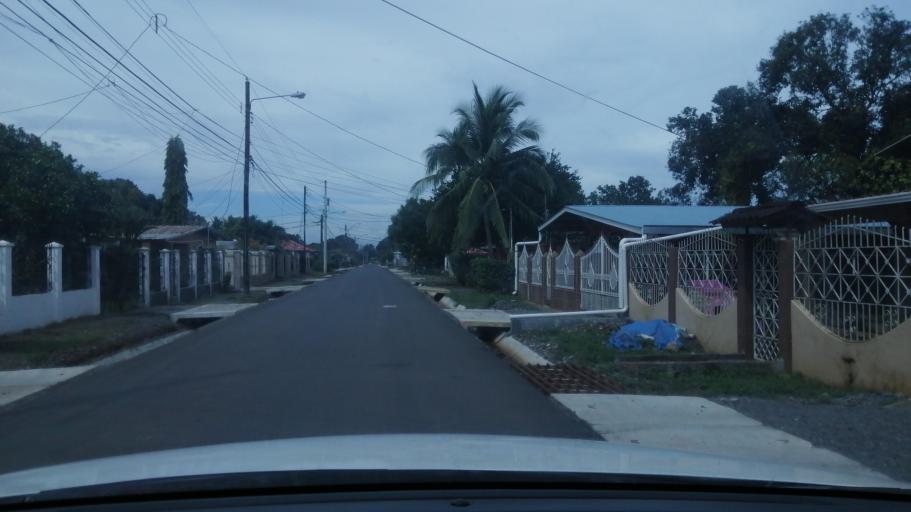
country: PA
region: Chiriqui
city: David
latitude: 8.4182
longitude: -82.4472
